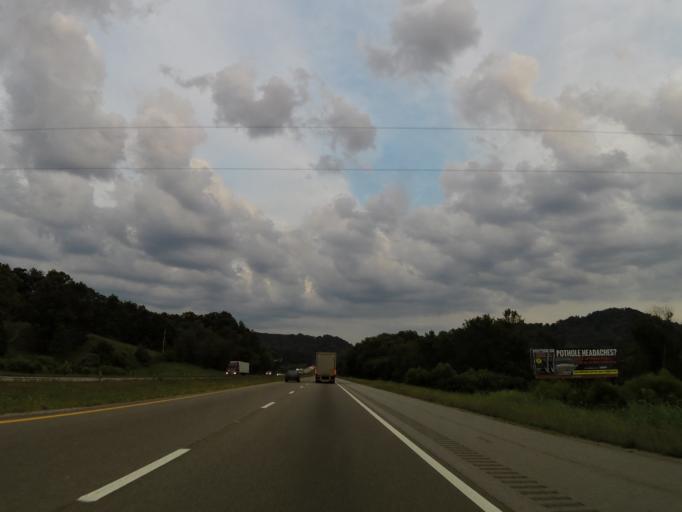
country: US
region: Tennessee
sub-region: Anderson County
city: Norris
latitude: 36.1438
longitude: -84.0519
